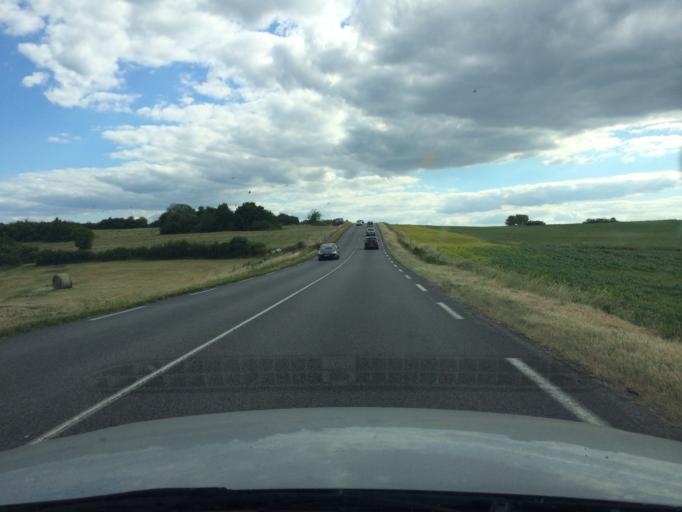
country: FR
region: Lorraine
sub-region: Departement de la Moselle
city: Lorquin
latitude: 48.6780
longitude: 6.9506
